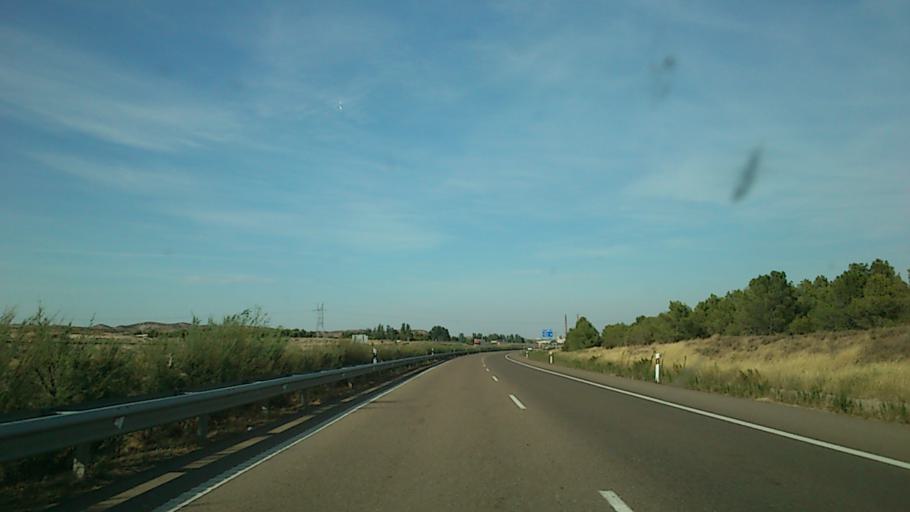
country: ES
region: Aragon
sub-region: Provincia de Zaragoza
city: Cuarte de Huerva
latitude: 41.5834
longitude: -0.9556
